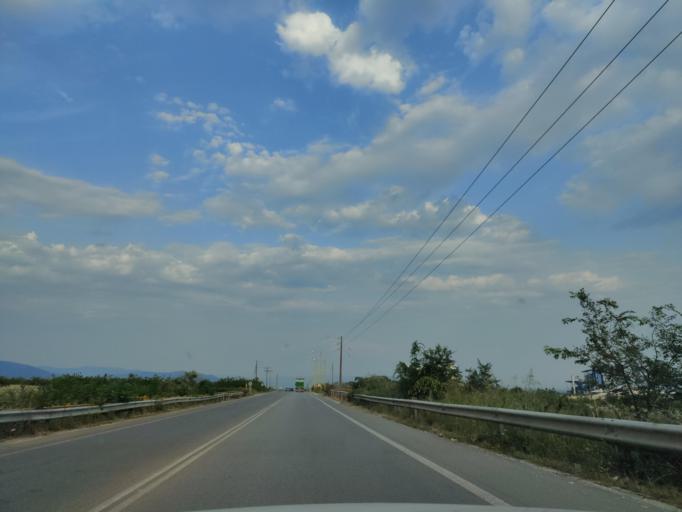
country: GR
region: East Macedonia and Thrace
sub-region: Nomos Dramas
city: Petroussa
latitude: 41.1763
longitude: 24.0075
